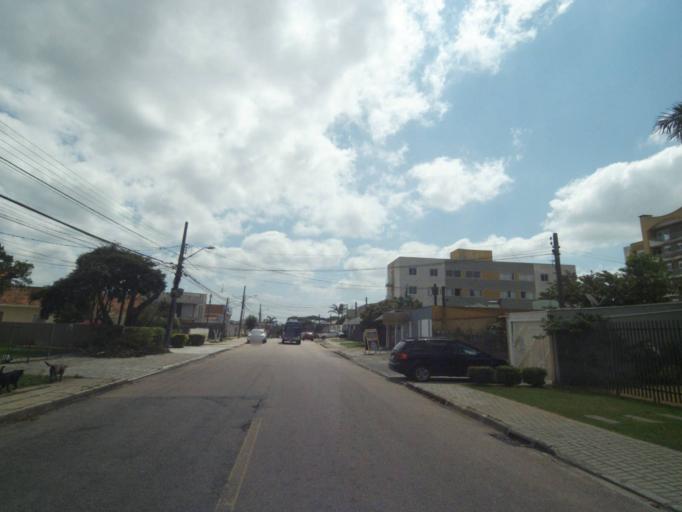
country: BR
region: Parana
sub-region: Curitiba
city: Curitiba
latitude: -25.5024
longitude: -49.2999
